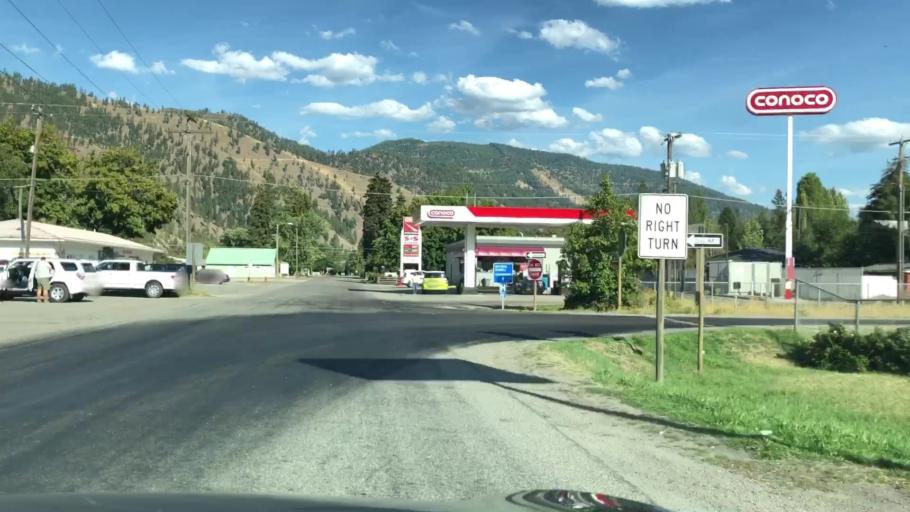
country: US
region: Montana
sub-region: Mineral County
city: Superior
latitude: 47.1925
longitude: -114.8897
